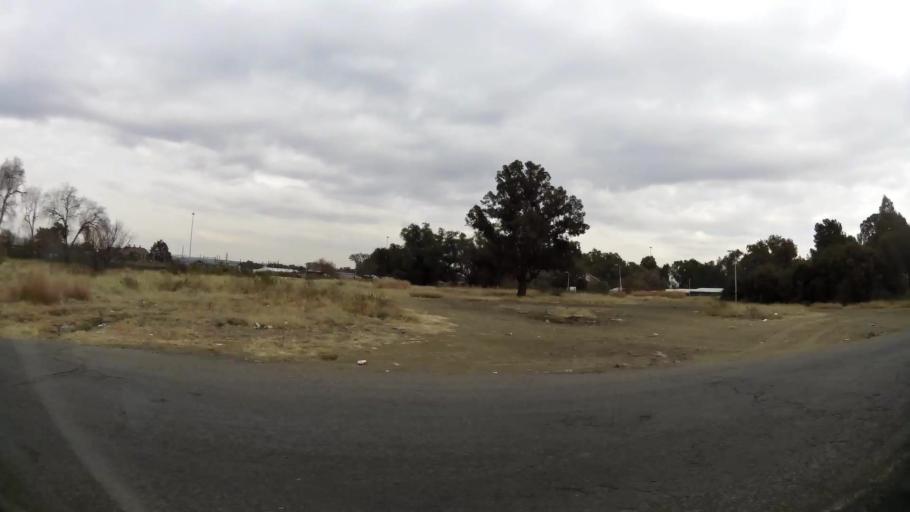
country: ZA
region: Orange Free State
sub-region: Fezile Dabi District Municipality
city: Kroonstad
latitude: -27.6590
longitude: 27.2309
